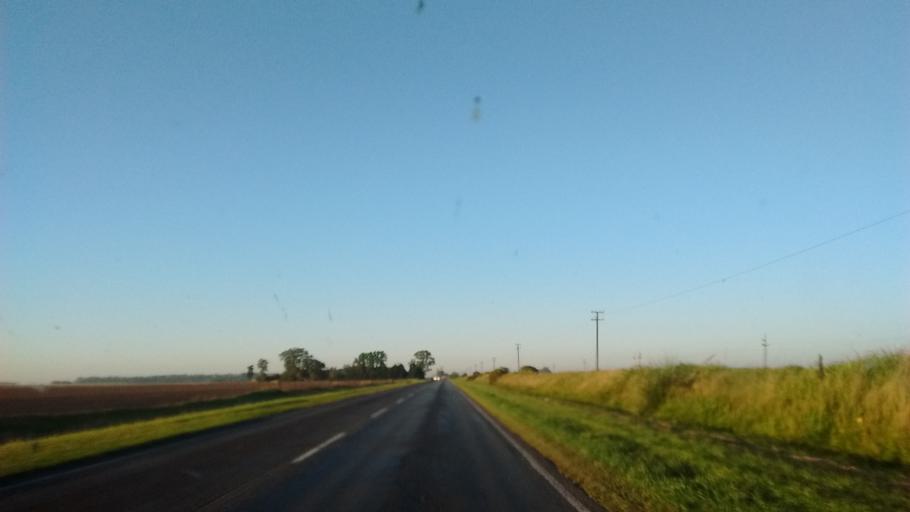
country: AR
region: Santa Fe
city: Casilda
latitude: -33.1086
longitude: -61.2501
